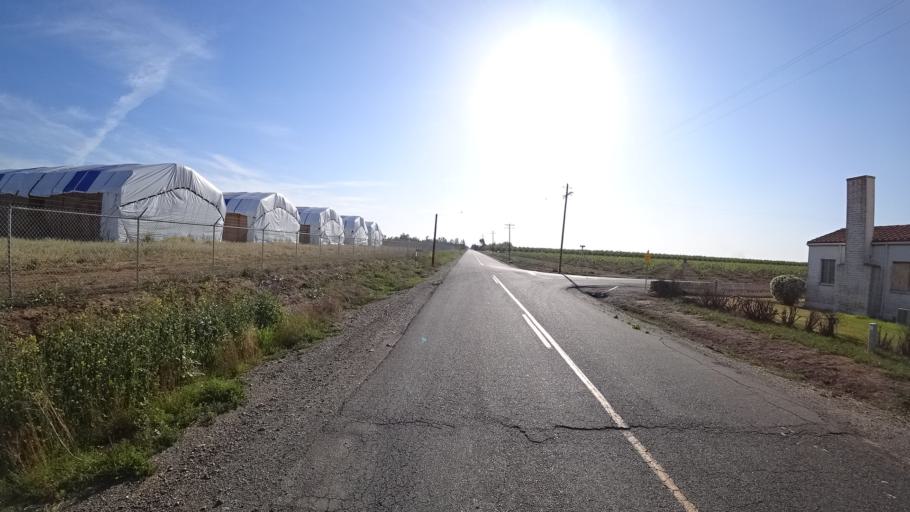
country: US
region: California
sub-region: Glenn County
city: Willows
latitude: 39.5095
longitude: -122.2359
